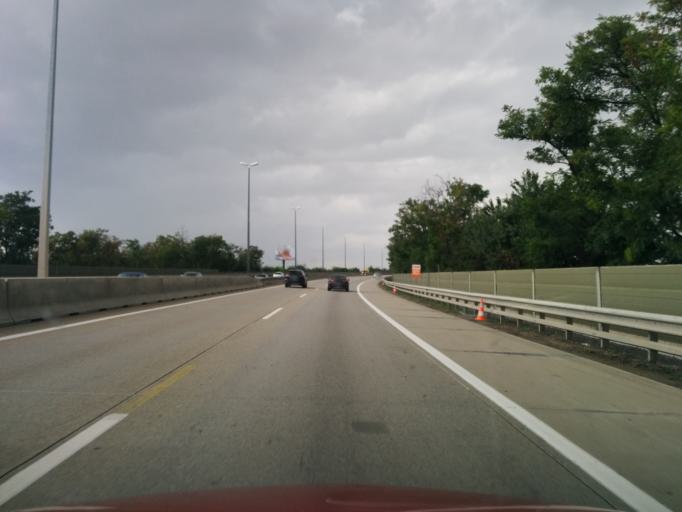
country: AT
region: Lower Austria
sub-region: Politischer Bezirk Wien-Umgebung
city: Schwechat
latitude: 48.1667
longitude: 16.4627
